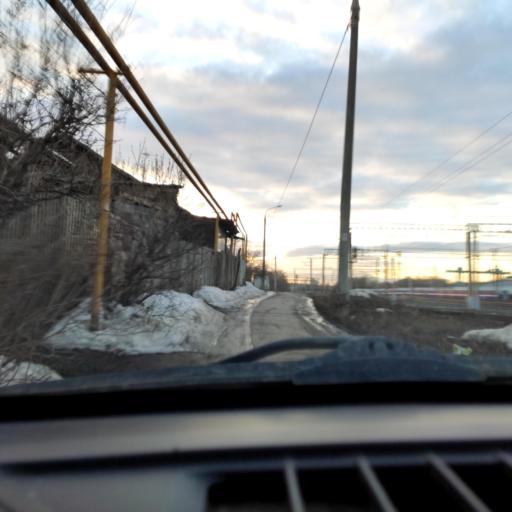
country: RU
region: Samara
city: Samara
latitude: 53.1724
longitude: 50.1623
